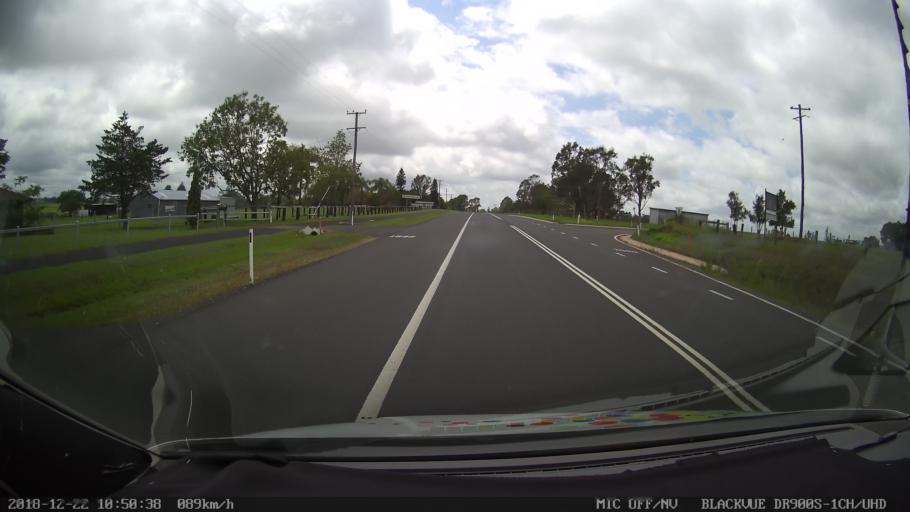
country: AU
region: New South Wales
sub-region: Clarence Valley
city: South Grafton
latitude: -29.6844
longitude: 152.8858
